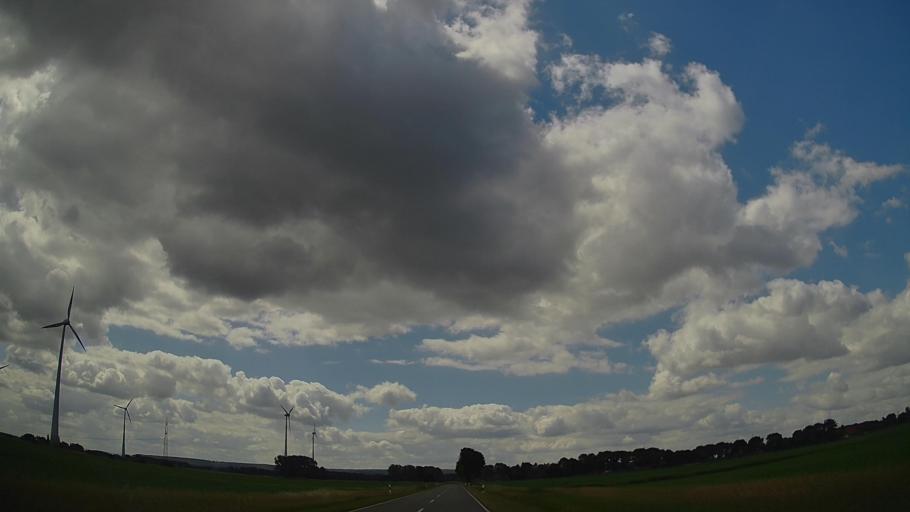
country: DE
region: Lower Saxony
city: Brockum
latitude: 52.5120
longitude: 8.4218
